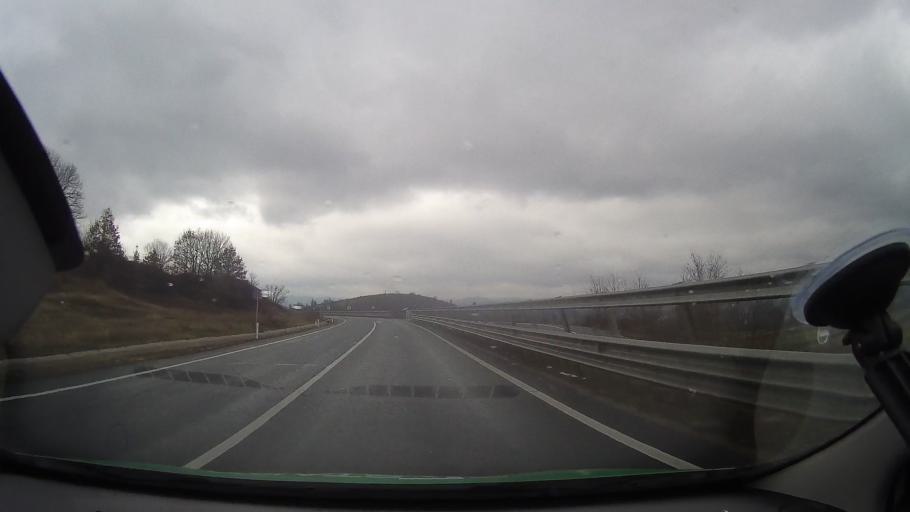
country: RO
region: Hunedoara
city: Vata de Jos
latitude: 46.2099
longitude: 22.5801
